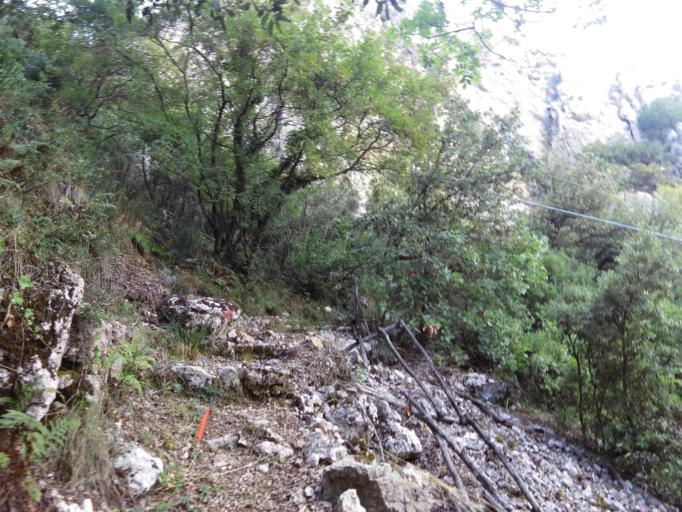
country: IT
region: Calabria
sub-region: Provincia di Reggio Calabria
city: Pazzano
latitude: 38.4719
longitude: 16.4500
